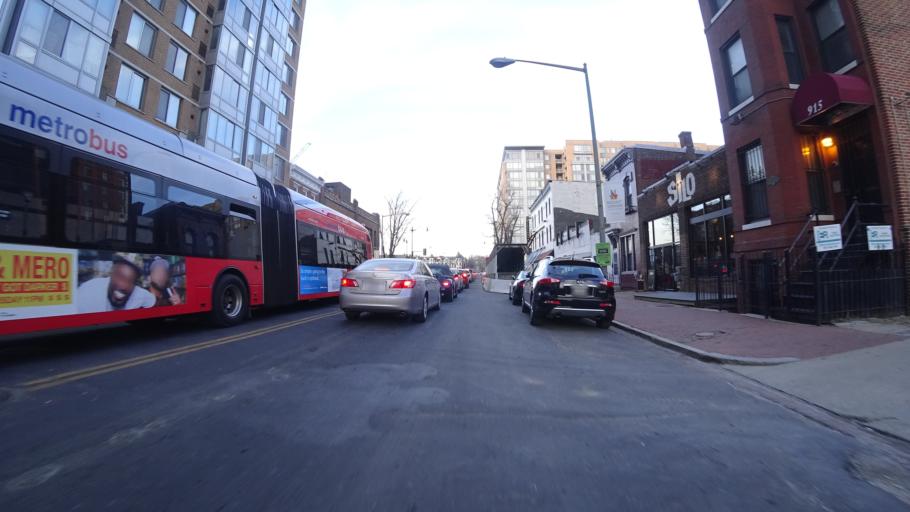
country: US
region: Washington, D.C.
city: Washington, D.C.
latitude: 38.9018
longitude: -77.0189
